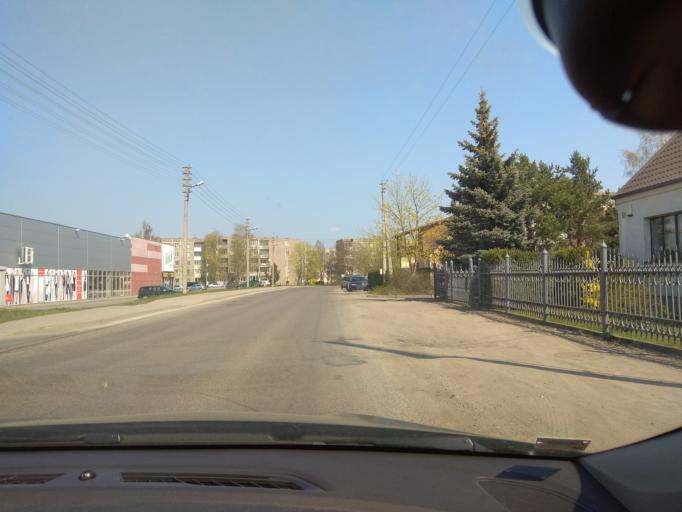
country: LT
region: Marijampoles apskritis
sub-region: Marijampole Municipality
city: Marijampole
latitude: 54.5662
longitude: 23.3506
